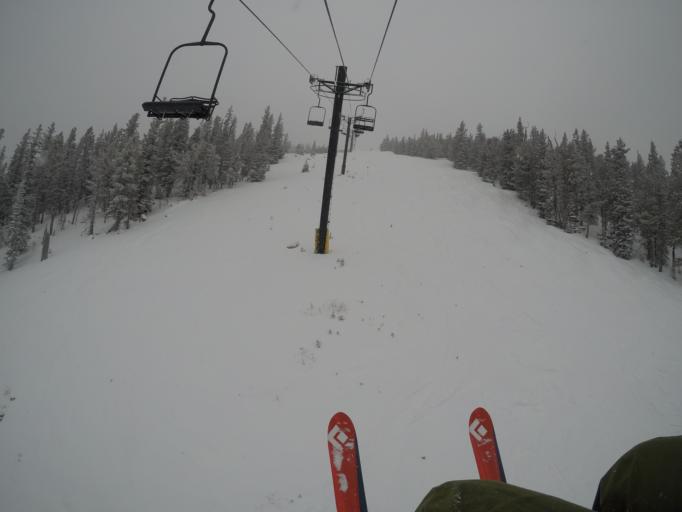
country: US
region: Montana
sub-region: Carbon County
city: Red Lodge
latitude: 45.1862
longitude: -109.3524
